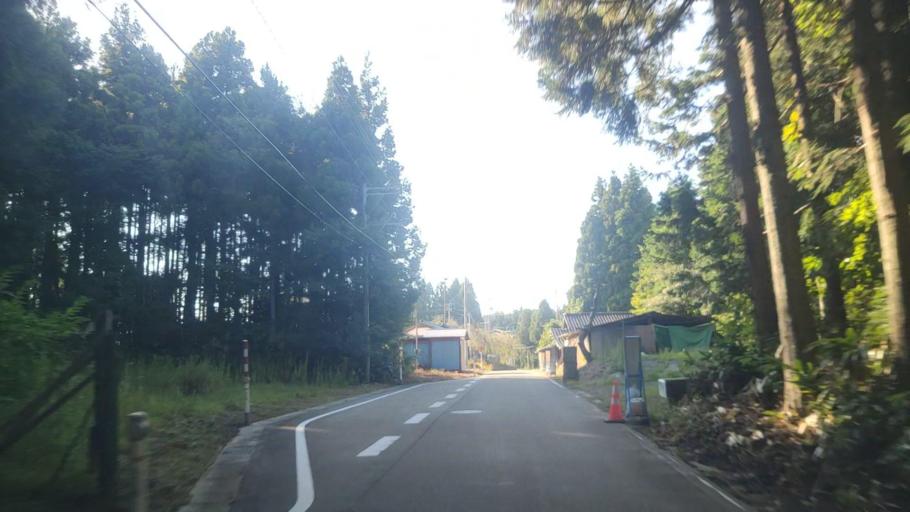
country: JP
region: Ishikawa
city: Nanao
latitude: 37.1305
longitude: 136.8930
